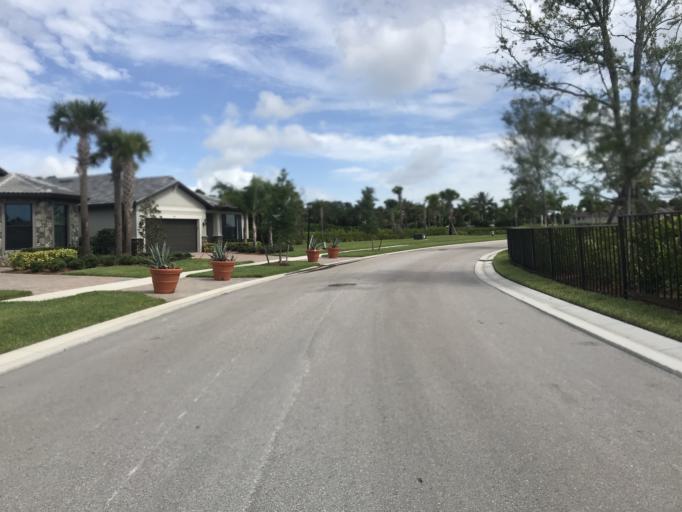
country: US
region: Florida
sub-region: Indian River County
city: Gifford
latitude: 27.6836
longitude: -80.4385
